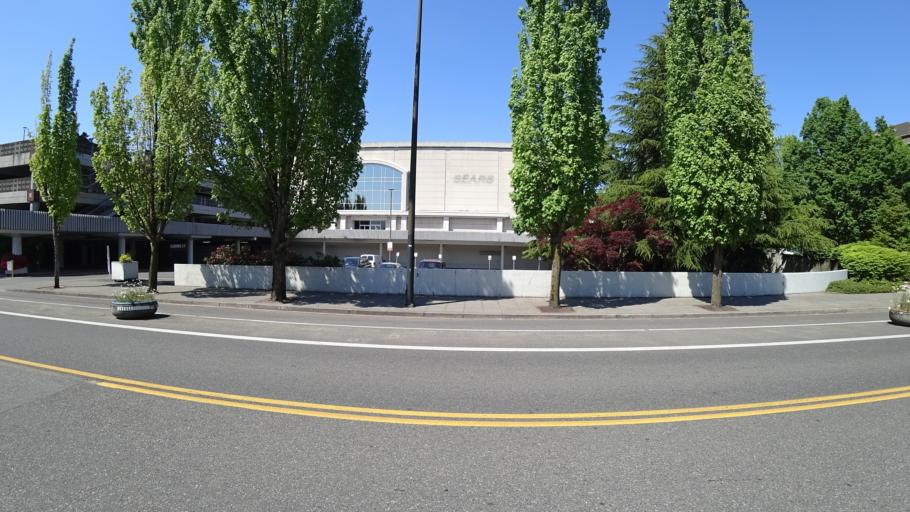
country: US
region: Oregon
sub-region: Multnomah County
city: Portland
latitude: 45.5315
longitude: -122.6512
